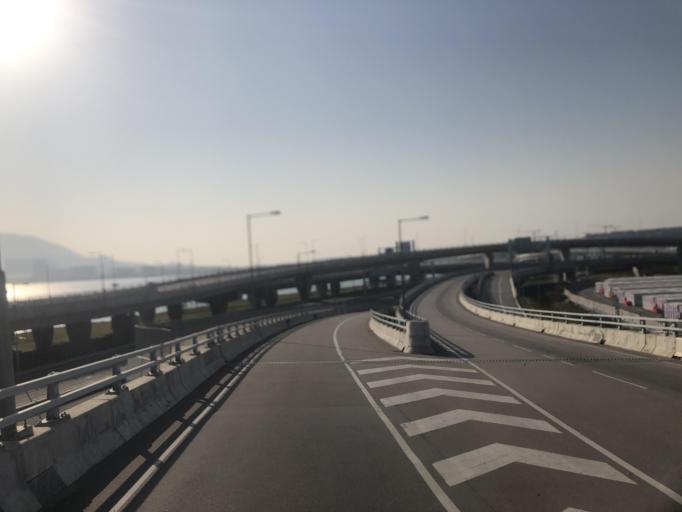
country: HK
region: Tuen Mun
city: Tuen Mun
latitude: 22.3121
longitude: 113.9562
